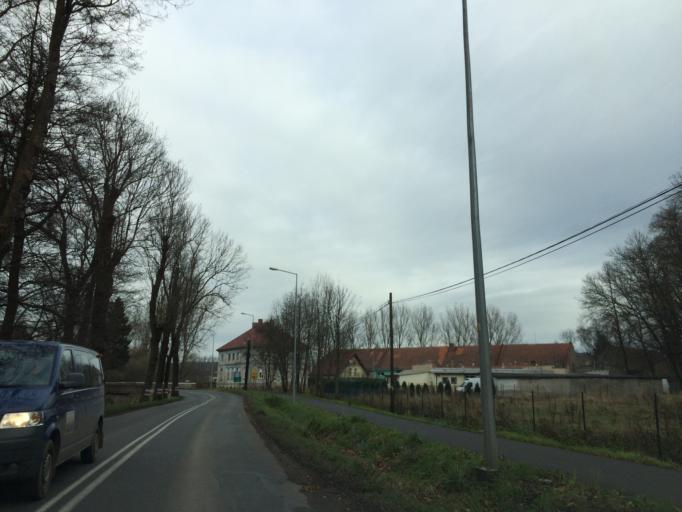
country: PL
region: Lower Silesian Voivodeship
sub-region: Powiat lwowecki
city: Lwowek Slaski
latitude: 51.1032
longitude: 15.5942
